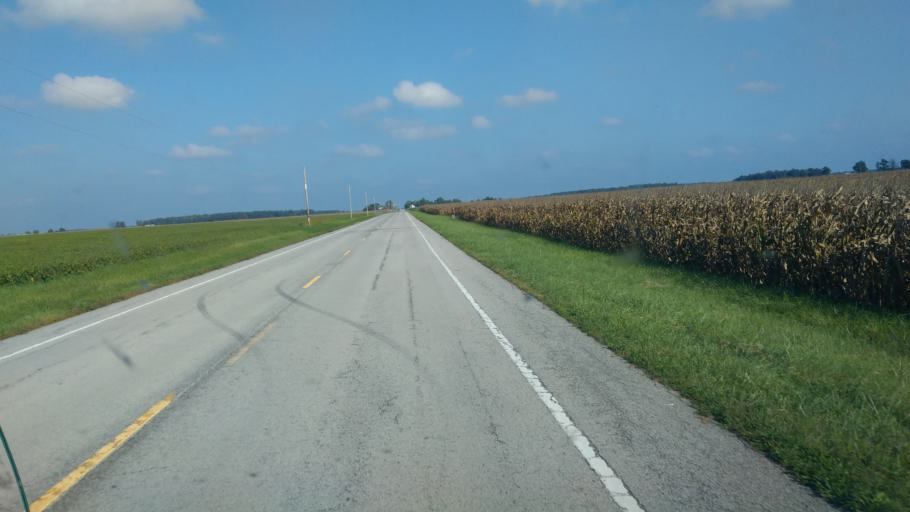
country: US
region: Ohio
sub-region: Hancock County
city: Arlington
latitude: 40.8339
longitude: -83.6225
